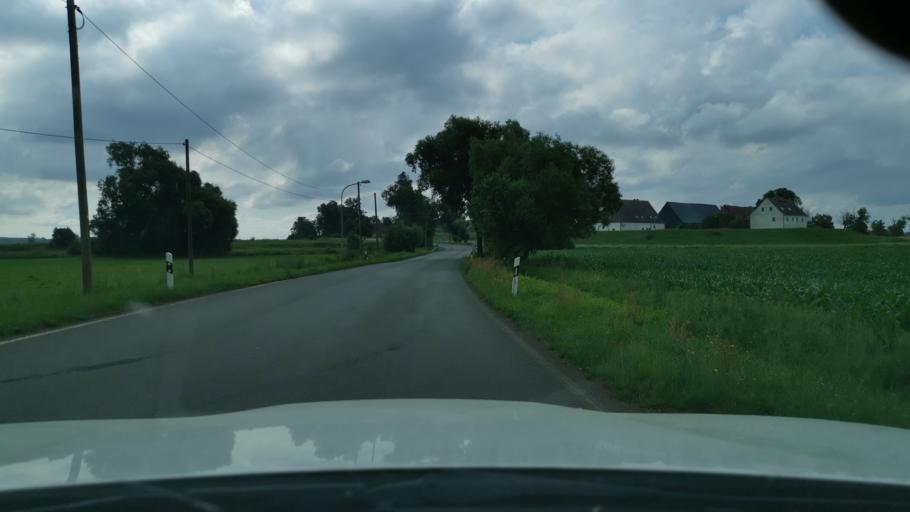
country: DE
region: Saxony
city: Torgau
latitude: 51.6165
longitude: 13.0133
